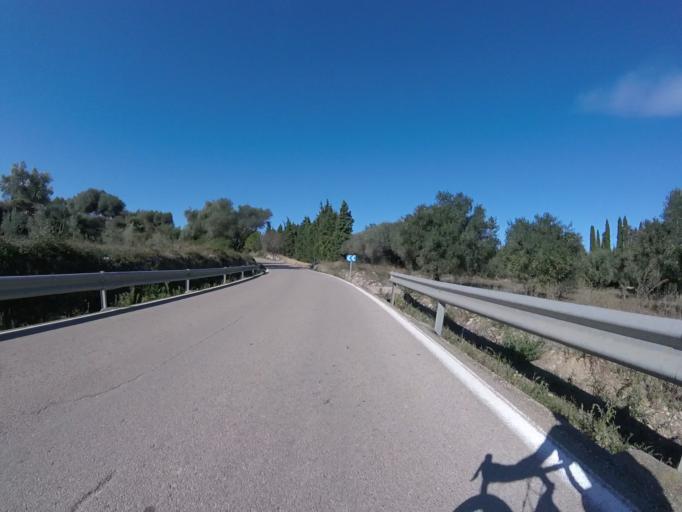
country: ES
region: Valencia
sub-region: Provincia de Castello
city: Chert/Xert
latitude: 40.4646
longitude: 0.1689
